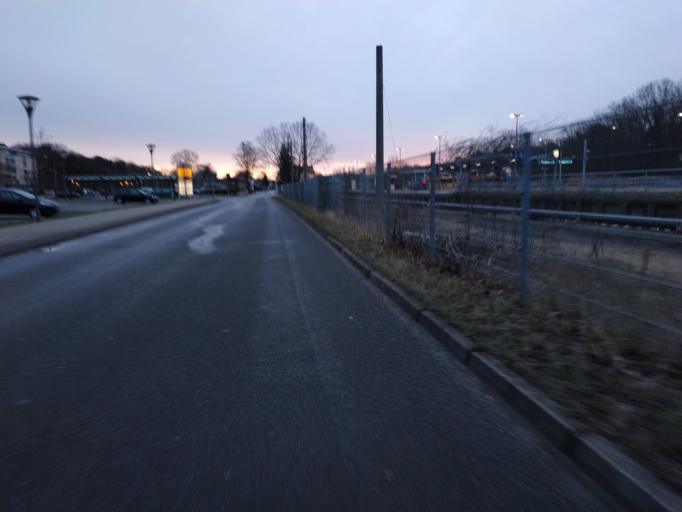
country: DE
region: Brandenburg
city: Petershagen
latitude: 52.5325
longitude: 13.8319
